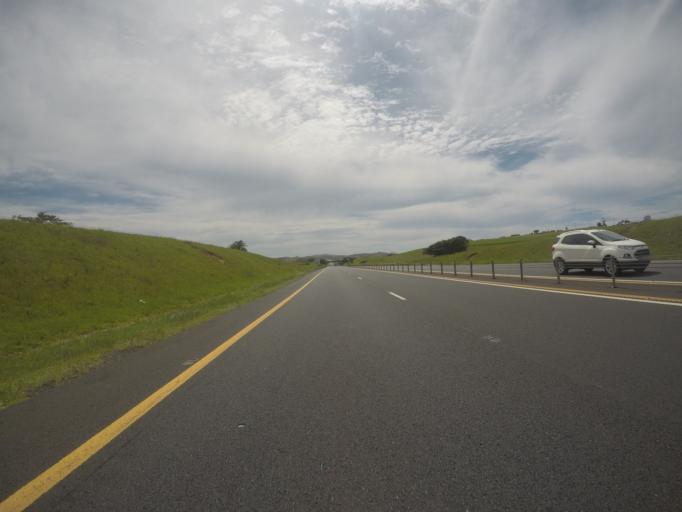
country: ZA
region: KwaZulu-Natal
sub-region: iLembe District Municipality
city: Mandeni
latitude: -29.1751
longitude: 31.5103
